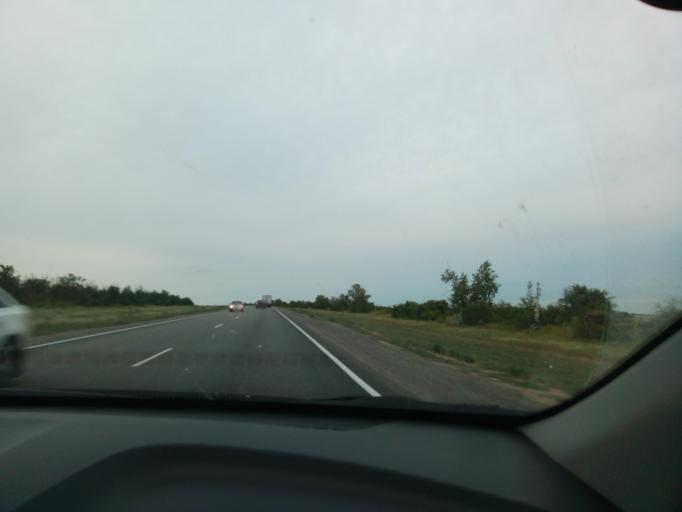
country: RU
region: Volgograd
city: Primorsk
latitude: 49.2076
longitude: 44.9001
